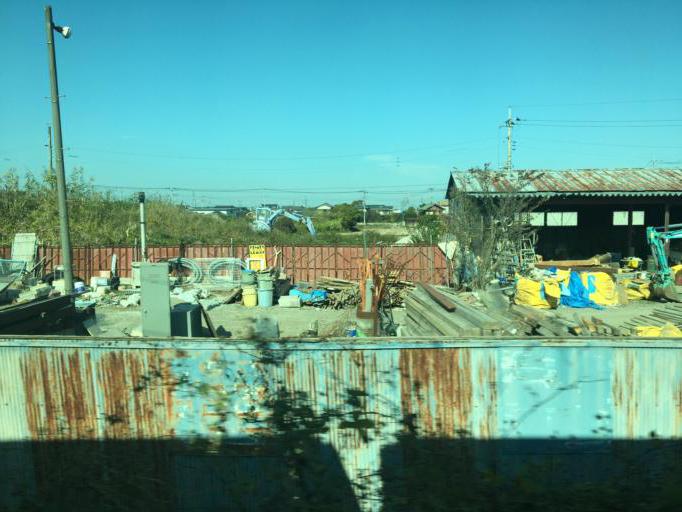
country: JP
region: Ibaraki
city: Yuki
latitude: 36.2969
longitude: 139.8901
